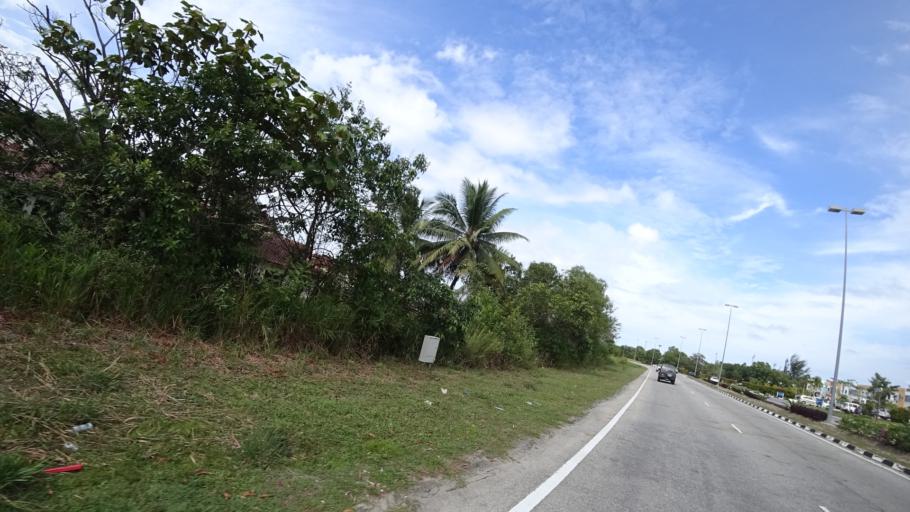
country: BN
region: Tutong
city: Tutong
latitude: 4.8125
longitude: 114.6548
